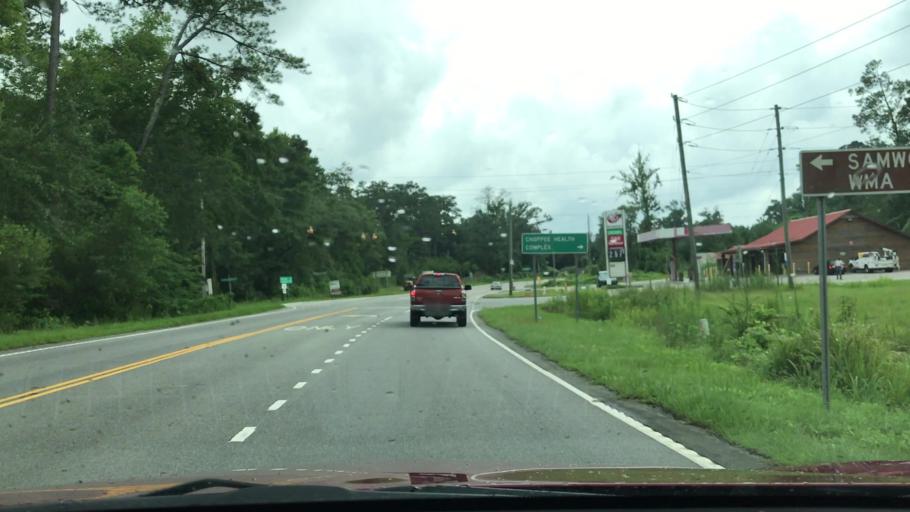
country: US
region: South Carolina
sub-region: Georgetown County
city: Georgetown
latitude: 33.4832
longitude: -79.2688
